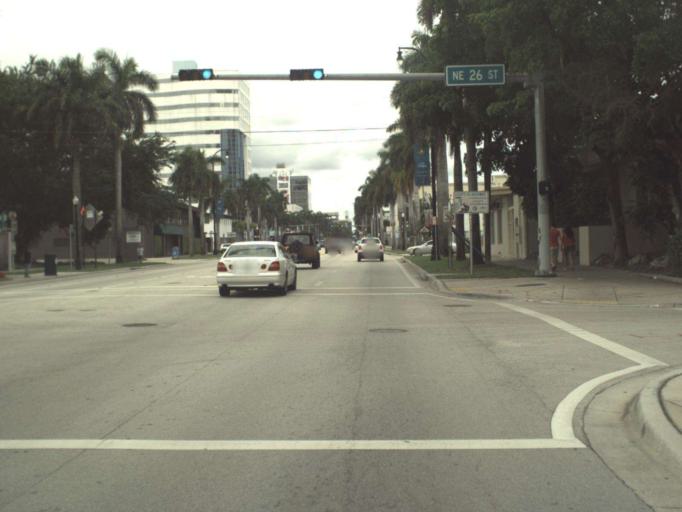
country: US
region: Florida
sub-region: Miami-Dade County
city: Miami
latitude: 25.8015
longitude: -80.1891
